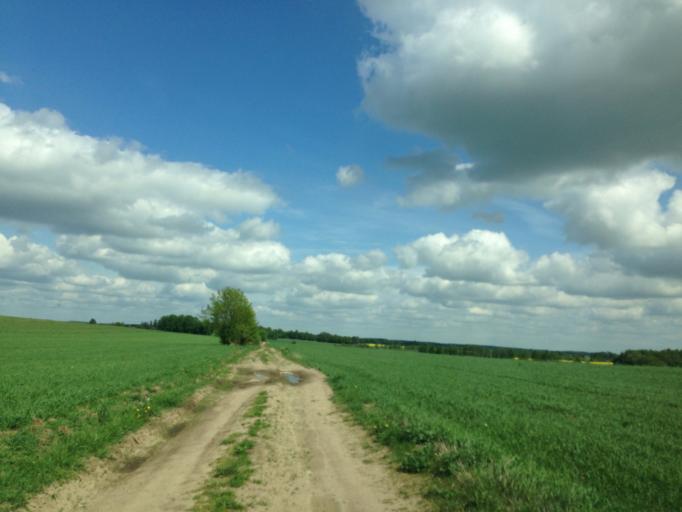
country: PL
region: Warmian-Masurian Voivodeship
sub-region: Powiat ostrodzki
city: Dabrowno
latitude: 53.3941
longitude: 20.1413
